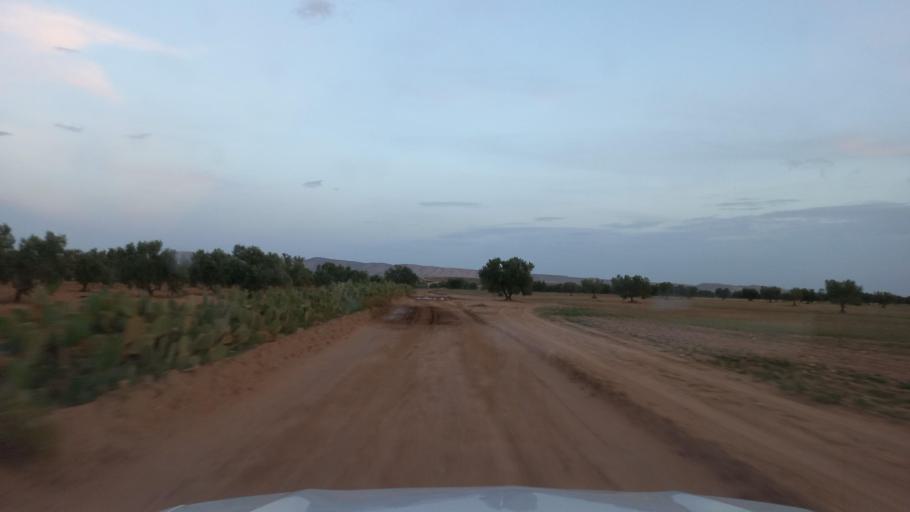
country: TN
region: Al Qasrayn
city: Sbiba
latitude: 35.3480
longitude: 9.0515
